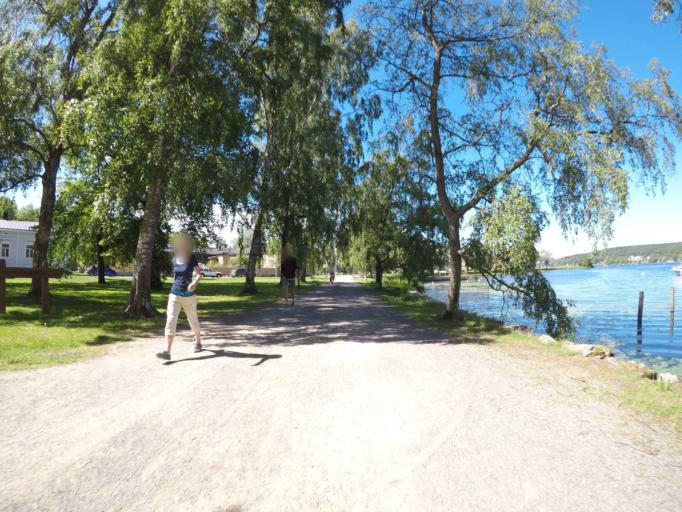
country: FI
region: Haeme
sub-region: Haemeenlinna
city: Haemeenlinna
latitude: 61.0004
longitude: 24.4645
